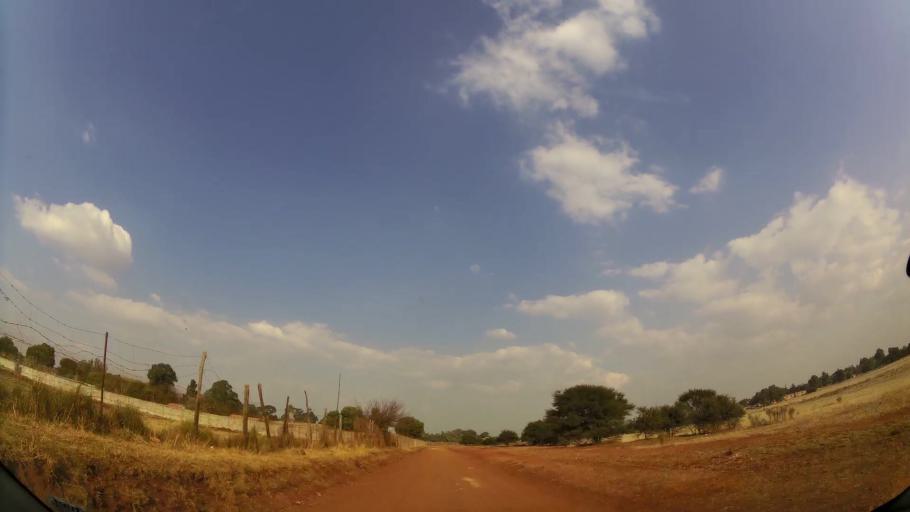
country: ZA
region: Gauteng
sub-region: Ekurhuleni Metropolitan Municipality
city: Benoni
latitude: -26.0964
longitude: 28.2860
